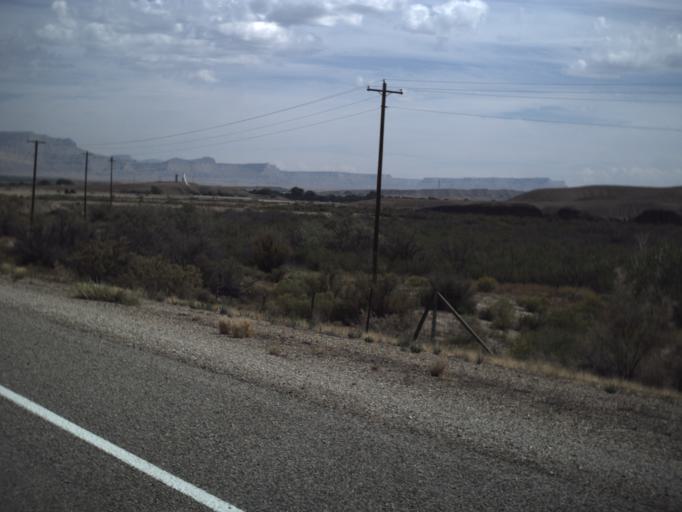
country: US
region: Utah
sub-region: Carbon County
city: East Carbon City
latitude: 38.9905
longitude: -110.1858
